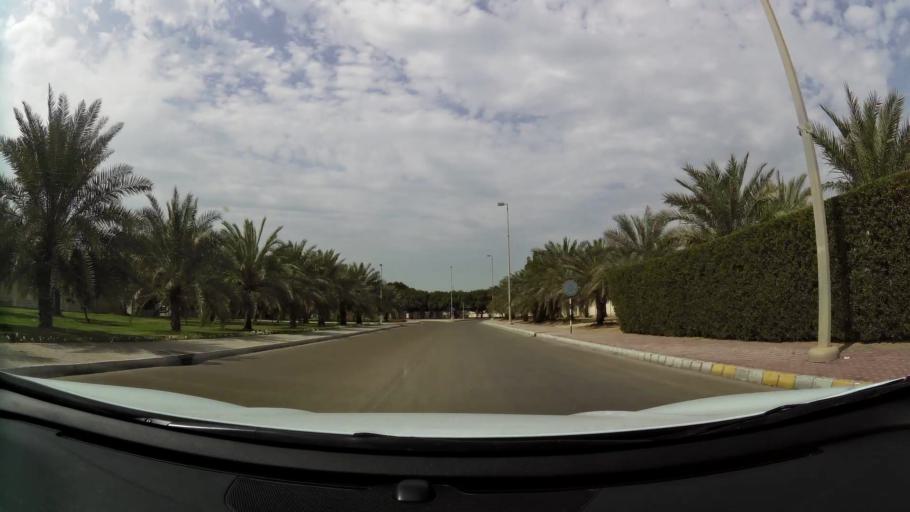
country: AE
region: Abu Dhabi
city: Abu Dhabi
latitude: 24.4486
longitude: 54.3488
